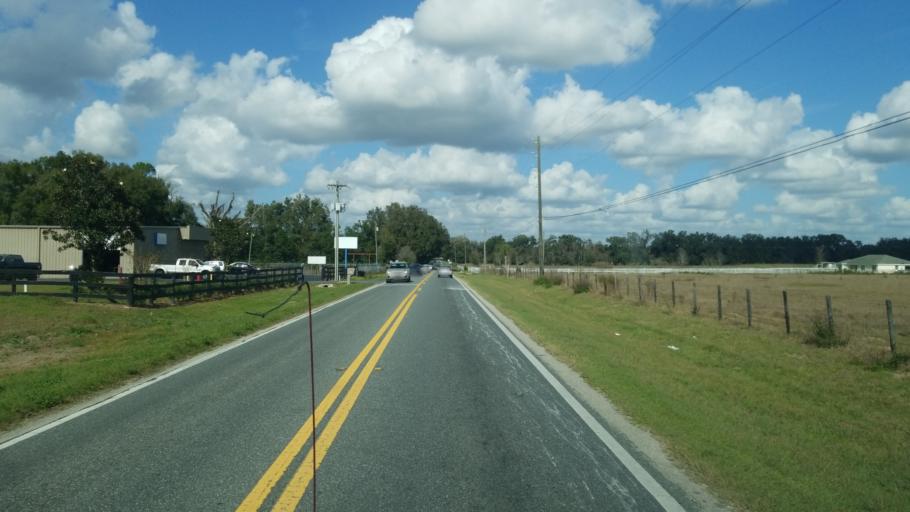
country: US
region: Florida
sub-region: Marion County
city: Belleview
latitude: 28.9841
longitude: -82.1199
